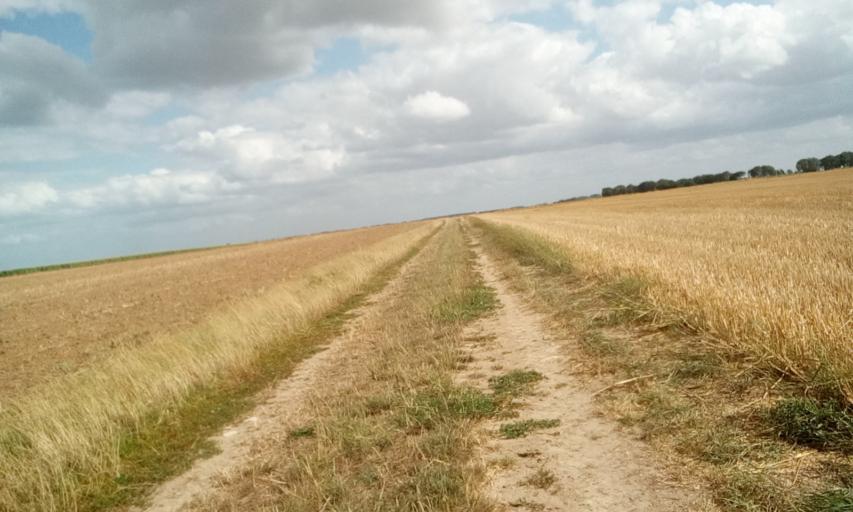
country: FR
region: Lower Normandy
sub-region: Departement du Calvados
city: Ver-sur-Mer
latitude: 49.3309
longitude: -0.5163
